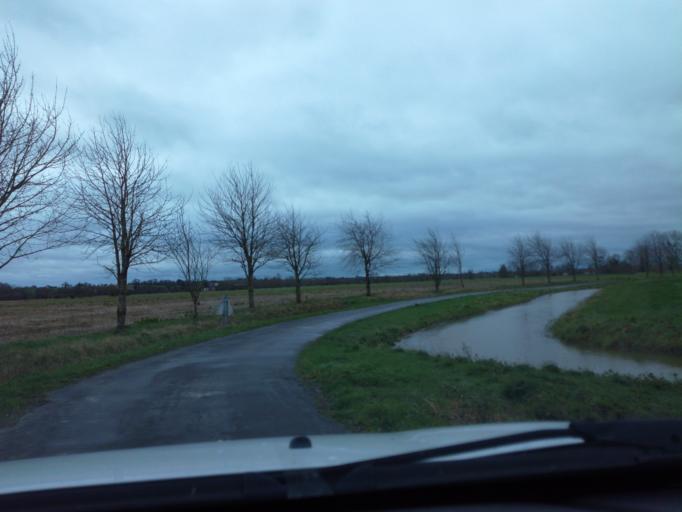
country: FR
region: Brittany
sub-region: Departement d'Ille-et-Vilaine
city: Baguer-Pican
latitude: 48.5780
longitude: -1.7134
